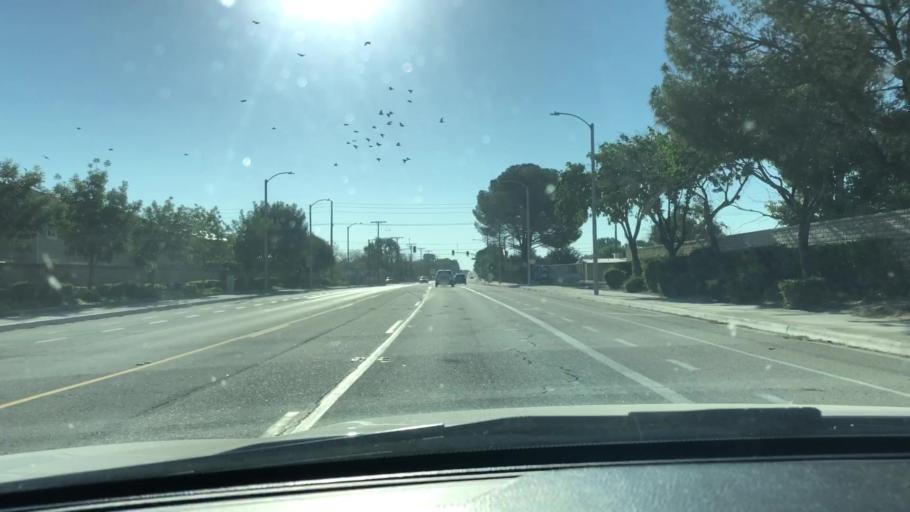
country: US
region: California
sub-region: Los Angeles County
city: Lancaster
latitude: 34.6676
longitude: -118.1677
